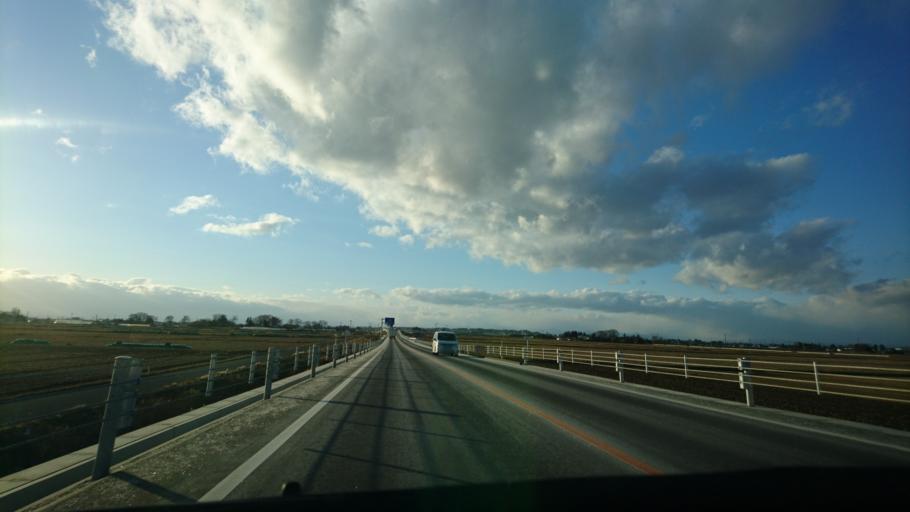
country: JP
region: Miyagi
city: Wakuya
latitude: 38.6854
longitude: 141.2446
